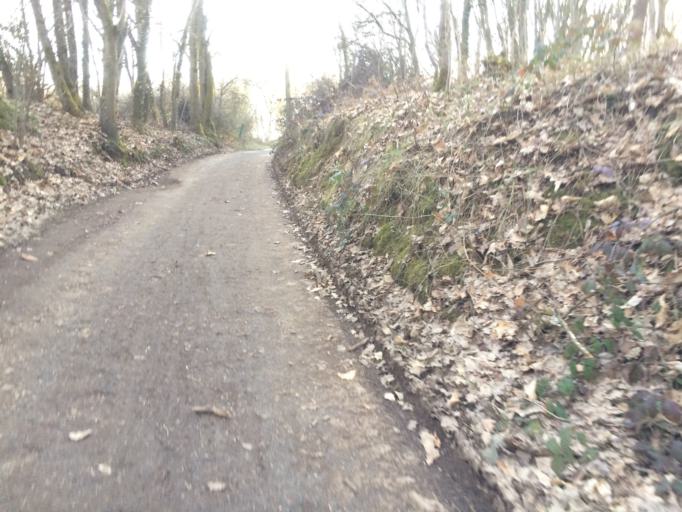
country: FR
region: Ile-de-France
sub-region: Departement de l'Essonne
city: Vauhallan
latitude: 48.7298
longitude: 2.2136
